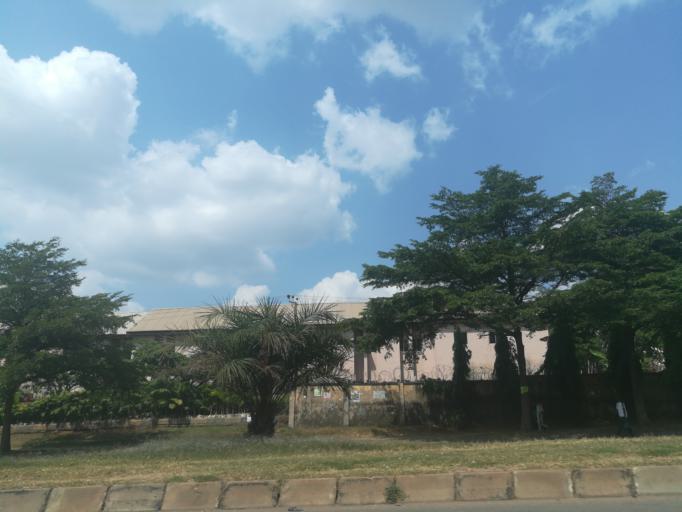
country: NG
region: Abuja Federal Capital Territory
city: Abuja
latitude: 9.0676
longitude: 7.4482
